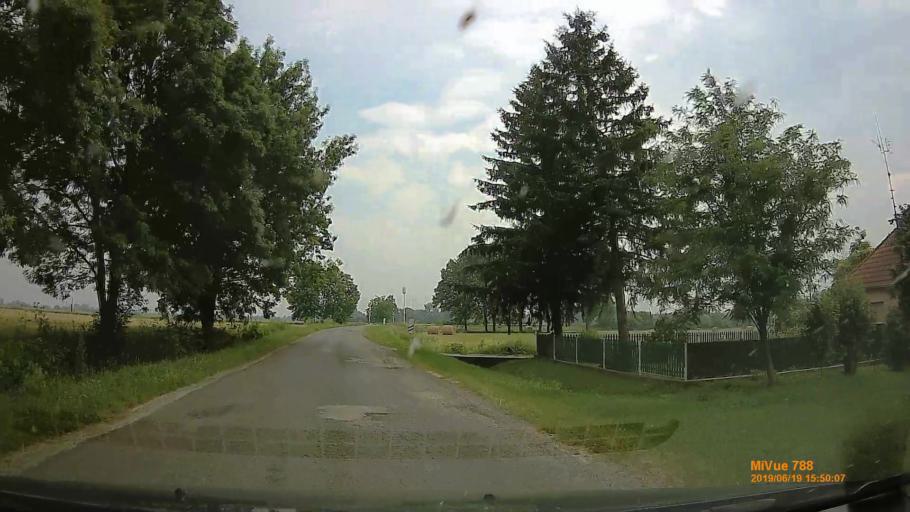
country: HU
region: Baranya
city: Szigetvar
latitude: 46.0366
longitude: 17.7482
